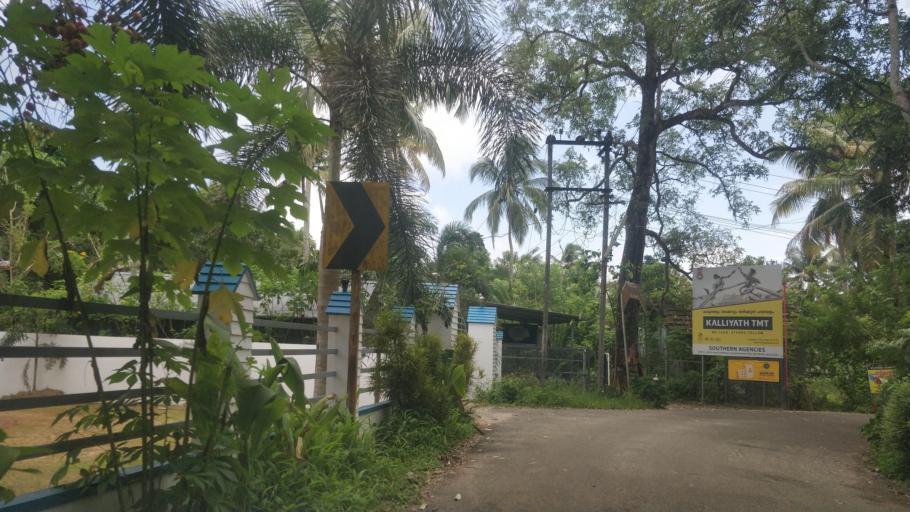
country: IN
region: Kerala
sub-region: Alappuzha
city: Shertallai
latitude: 9.6635
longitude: 76.3758
